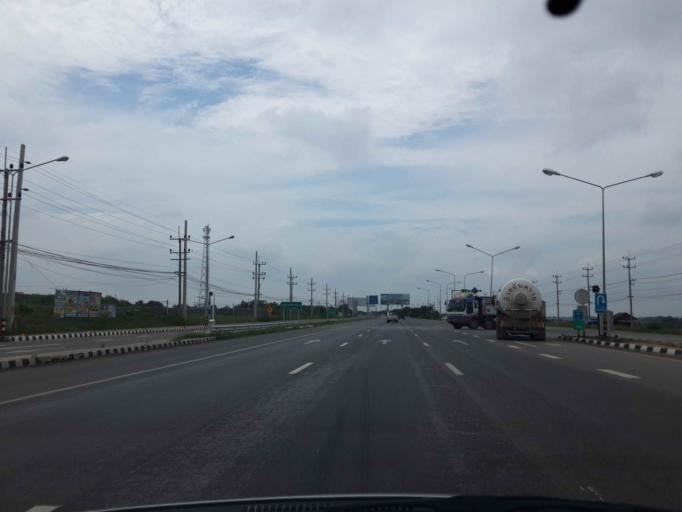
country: TH
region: Samut Songkhram
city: Samut Songkhram
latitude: 13.4282
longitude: 100.0435
